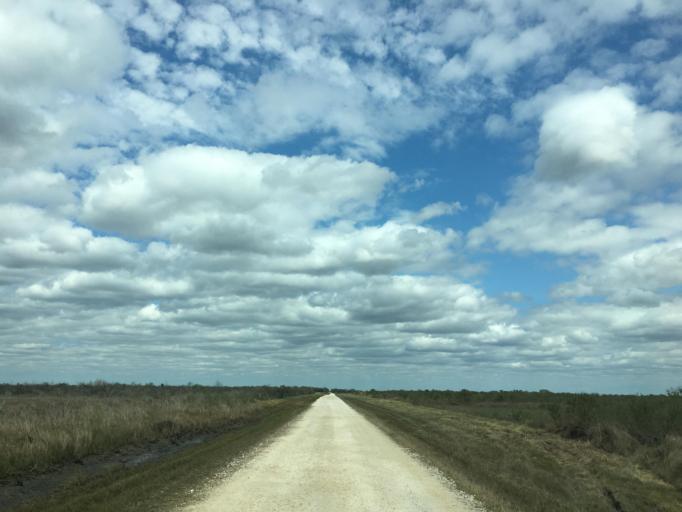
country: US
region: Texas
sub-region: Brazoria County
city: Oyster Creek
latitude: 29.0454
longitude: -95.2682
